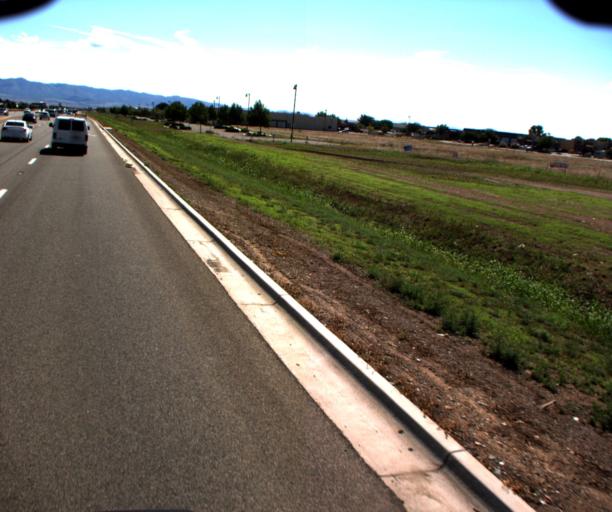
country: US
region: Arizona
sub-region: Yavapai County
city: Prescott Valley
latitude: 34.5804
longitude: -112.3557
